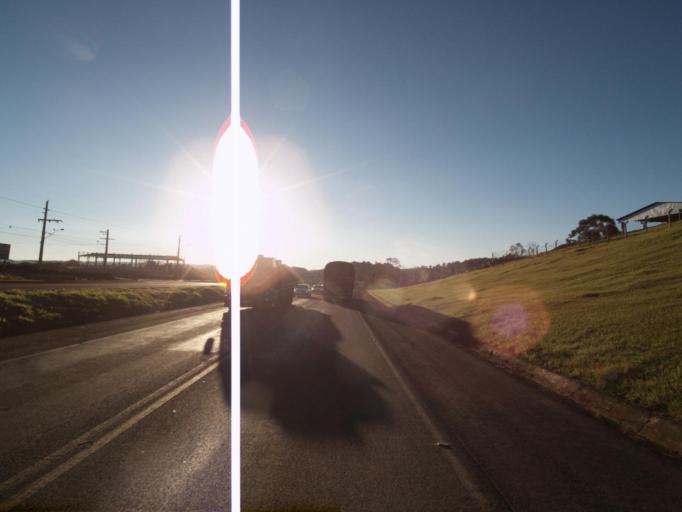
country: BR
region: Santa Catarina
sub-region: Chapeco
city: Chapeco
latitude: -26.8344
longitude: -52.9919
